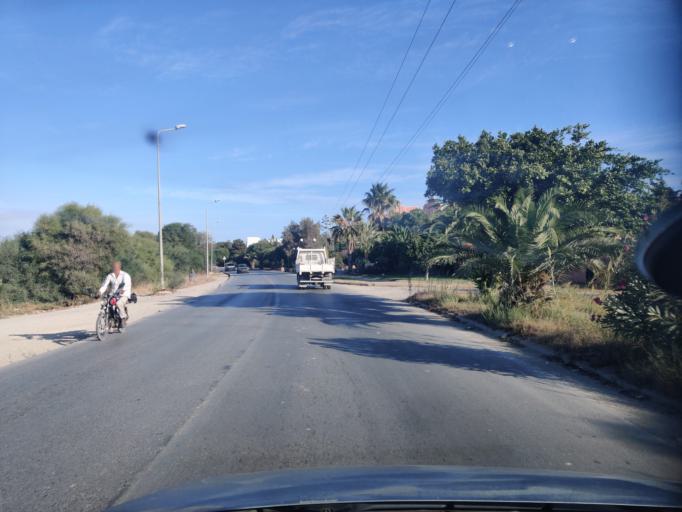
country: TN
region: Tunis
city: Al Marsa
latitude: 36.9380
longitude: 10.2526
